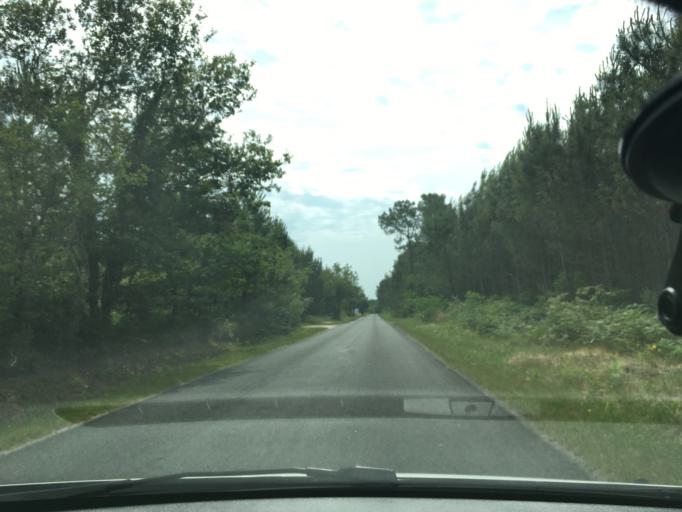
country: FR
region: Aquitaine
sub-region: Departement de la Gironde
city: Gaillan-en-Medoc
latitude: 45.3494
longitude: -1.0416
